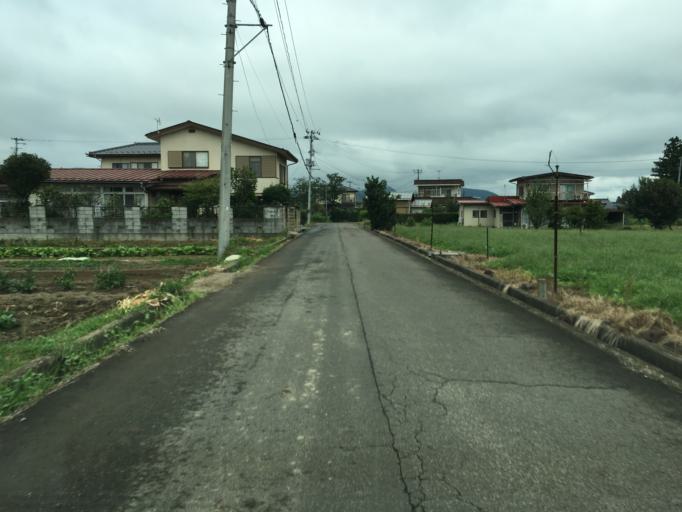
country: JP
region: Fukushima
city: Fukushima-shi
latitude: 37.7642
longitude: 140.3943
